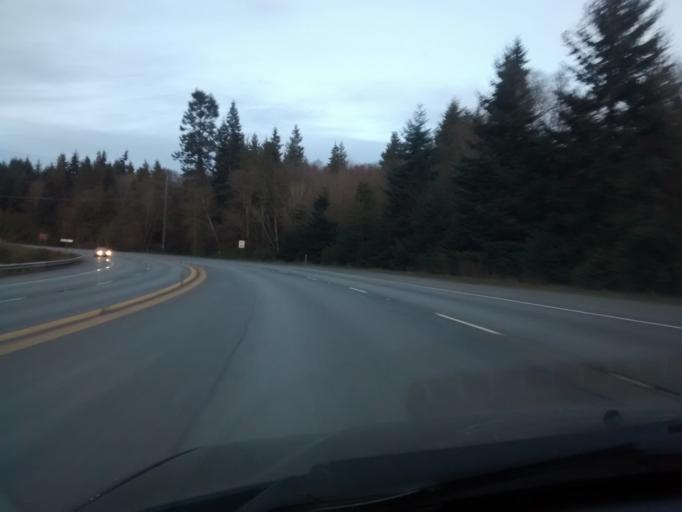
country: US
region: Washington
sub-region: Clallam County
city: Port Angeles East
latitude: 48.1029
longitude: -123.3544
